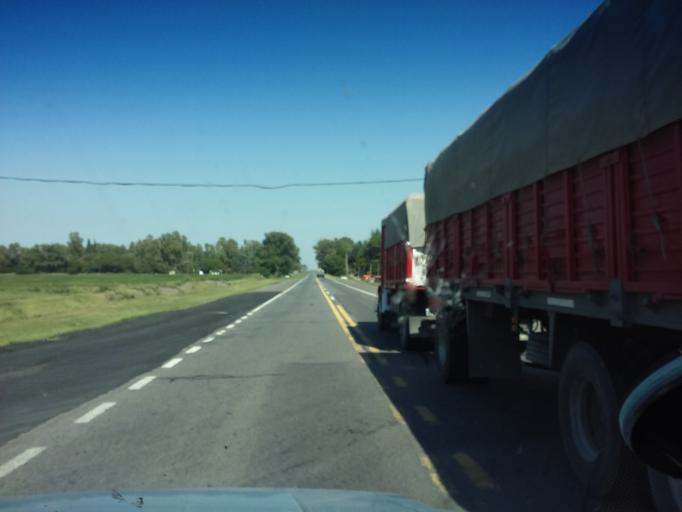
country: AR
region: Buenos Aires
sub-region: Partido de Alberti
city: Alberti
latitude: -35.0568
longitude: -60.2718
